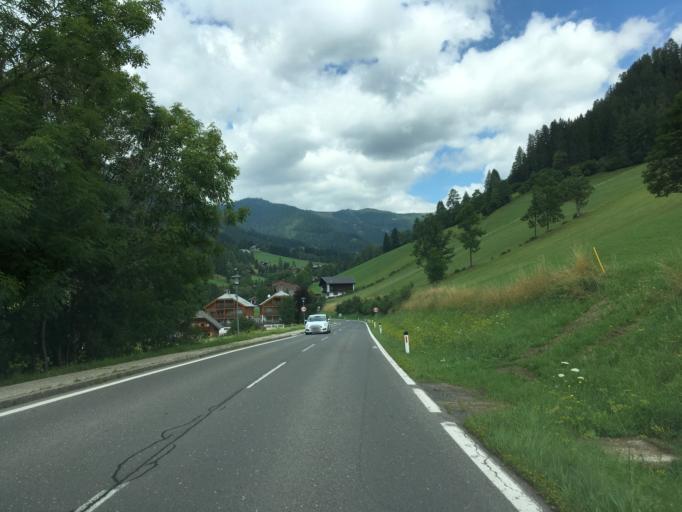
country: AT
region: Carinthia
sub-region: Politischer Bezirk Spittal an der Drau
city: Kleinkirchheim
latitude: 46.8176
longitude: 13.7755
